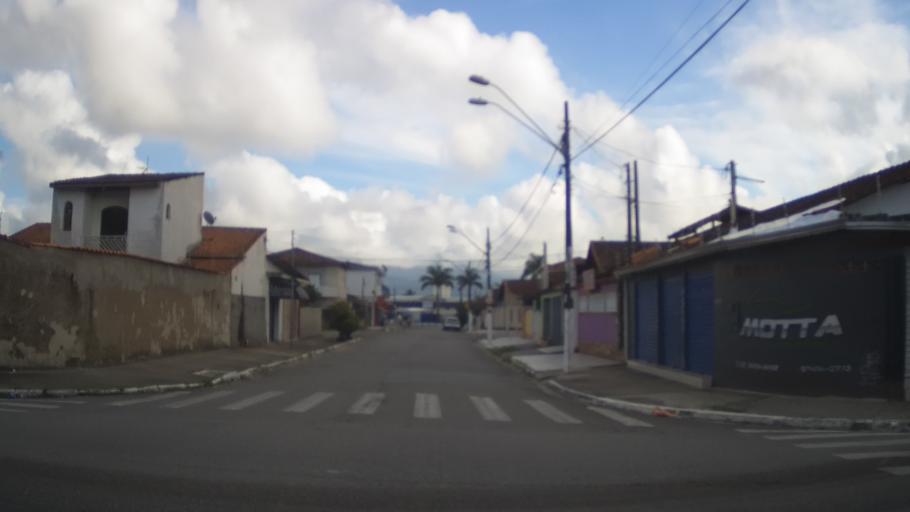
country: BR
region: Sao Paulo
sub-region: Praia Grande
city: Praia Grande
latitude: -24.0160
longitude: -46.4687
